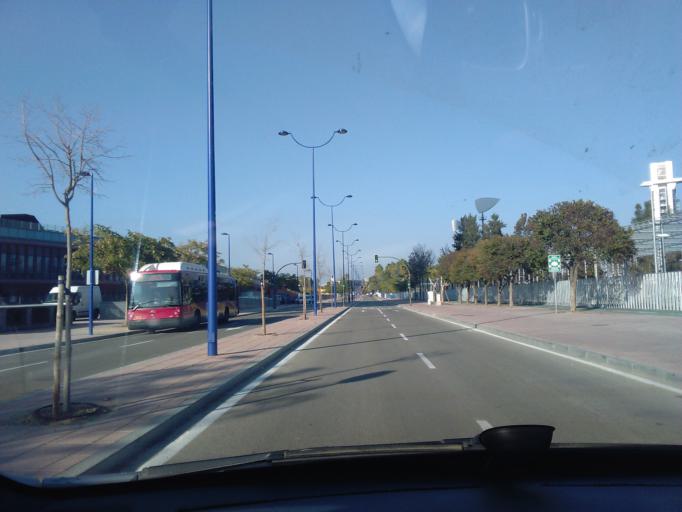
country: ES
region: Andalusia
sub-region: Provincia de Sevilla
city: Camas
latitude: 37.3913
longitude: -6.0093
